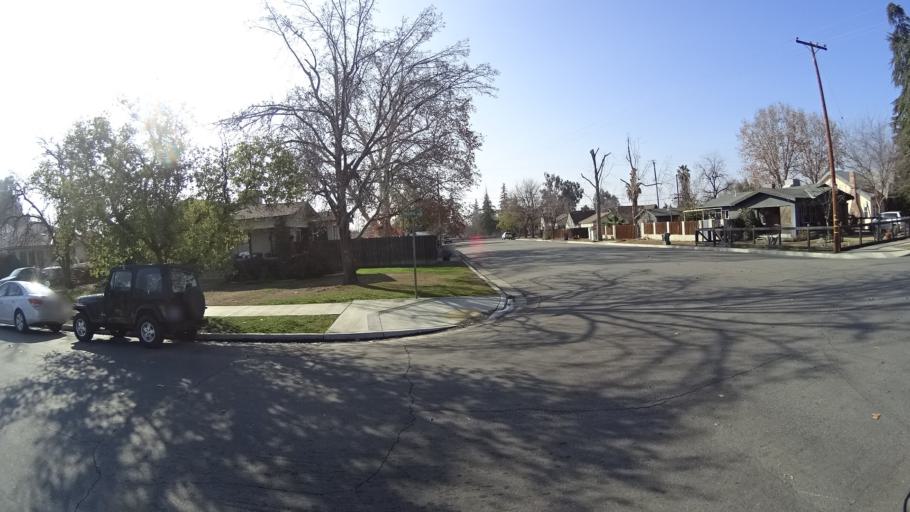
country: US
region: California
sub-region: Kern County
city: Bakersfield
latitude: 35.3853
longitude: -118.9948
